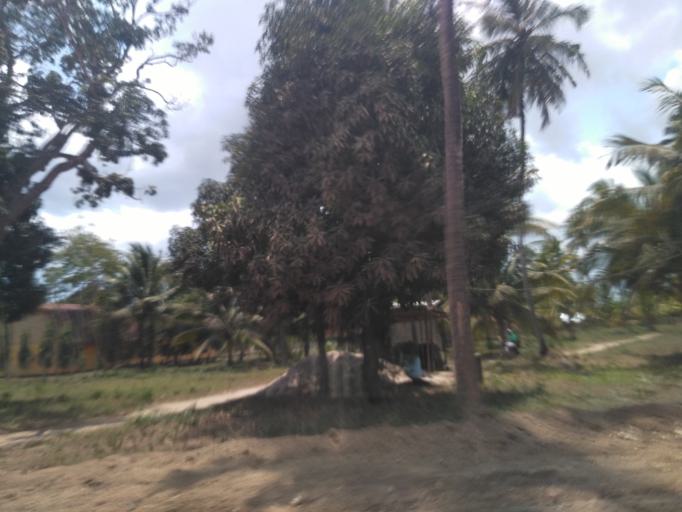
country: TZ
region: Dar es Salaam
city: Dar es Salaam
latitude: -6.8715
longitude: 39.3306
